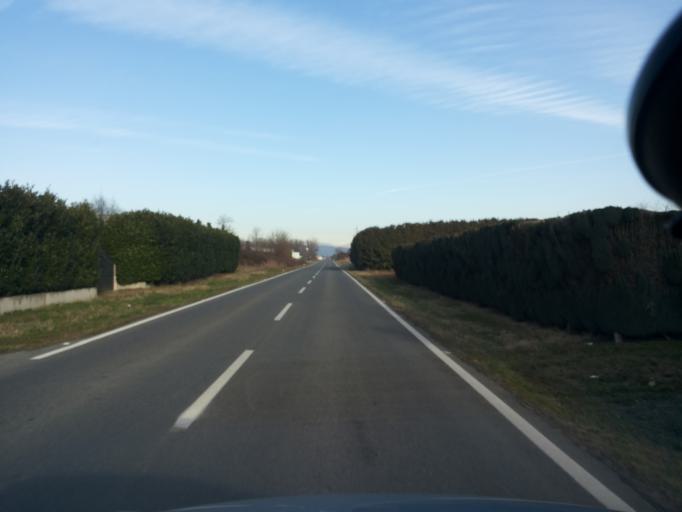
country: IT
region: Piedmont
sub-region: Provincia di Vercelli
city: Ghislarengo
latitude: 45.5378
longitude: 8.3855
